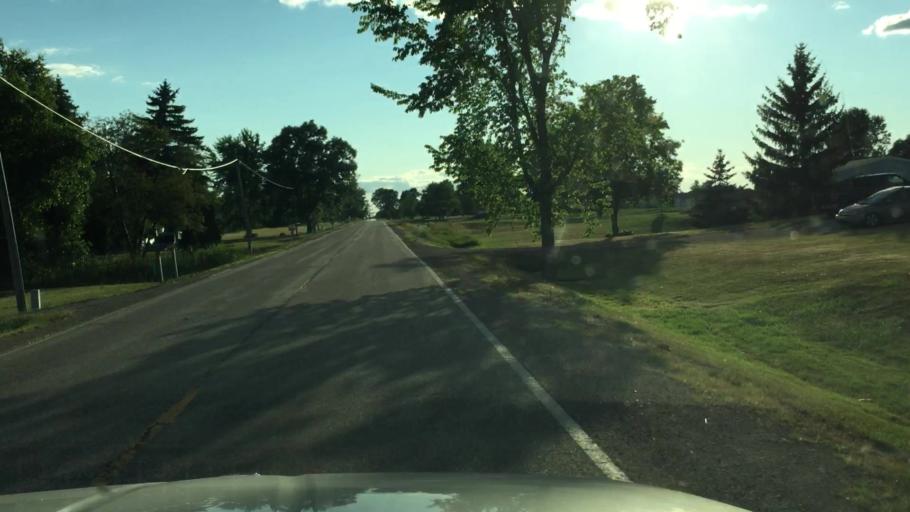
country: US
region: Michigan
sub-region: Saint Clair County
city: Capac
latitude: 43.0271
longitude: -82.9311
